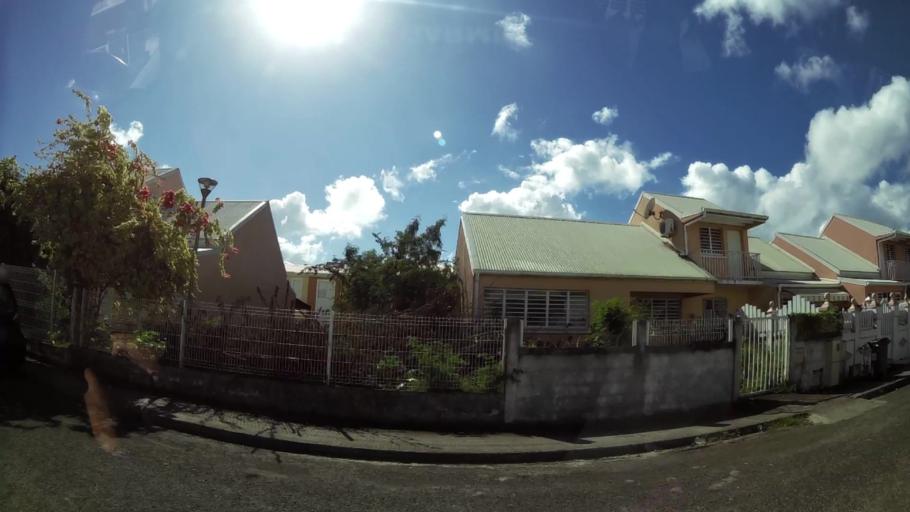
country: GP
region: Guadeloupe
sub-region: Guadeloupe
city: Port-Louis
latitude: 16.4124
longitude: -61.5283
